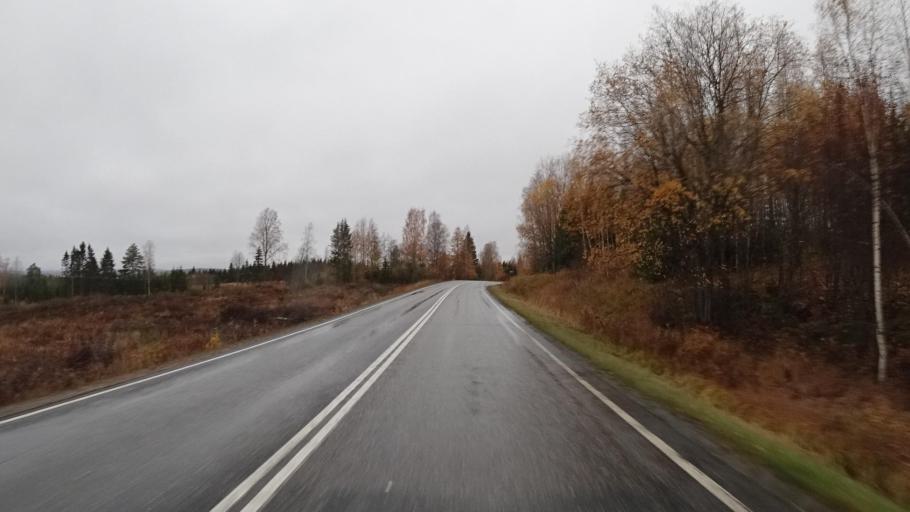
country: FI
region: Northern Savo
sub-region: Koillis-Savo
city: Tuusniemi
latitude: 62.7896
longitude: 28.5772
